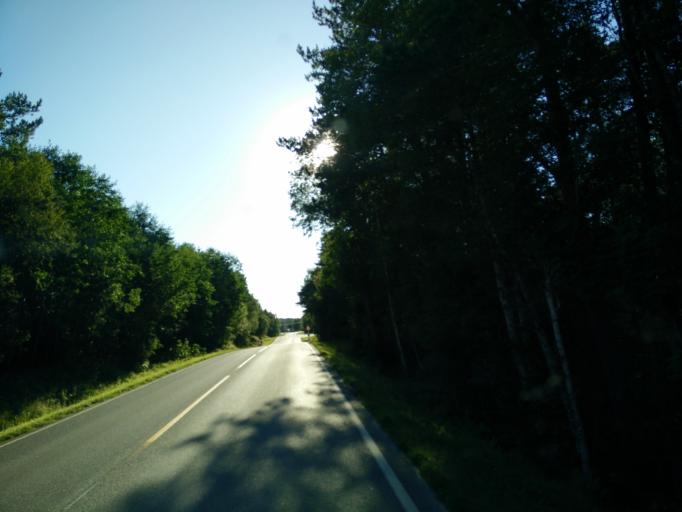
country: NO
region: More og Romsdal
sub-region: Halsa
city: Liaboen
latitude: 63.0725
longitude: 8.2906
